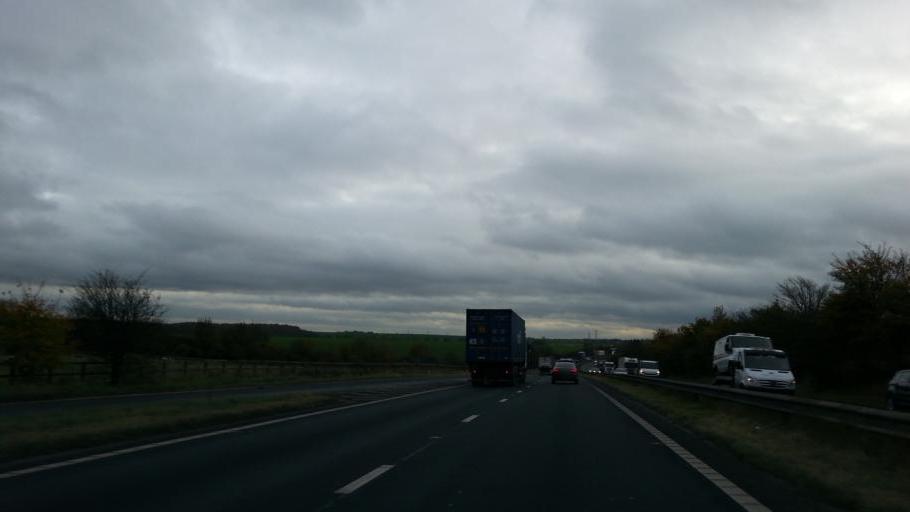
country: GB
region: England
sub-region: City and Borough of Wakefield
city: Darrington
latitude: 53.6760
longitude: -1.2612
